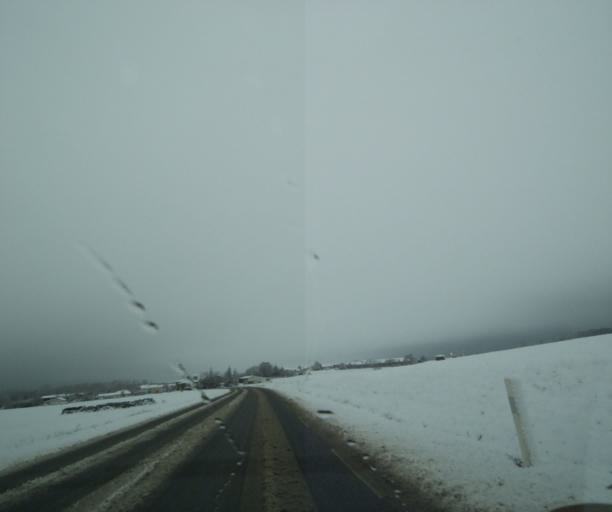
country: FR
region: Champagne-Ardenne
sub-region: Departement de la Haute-Marne
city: Wassy
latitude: 48.5207
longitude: 4.9336
